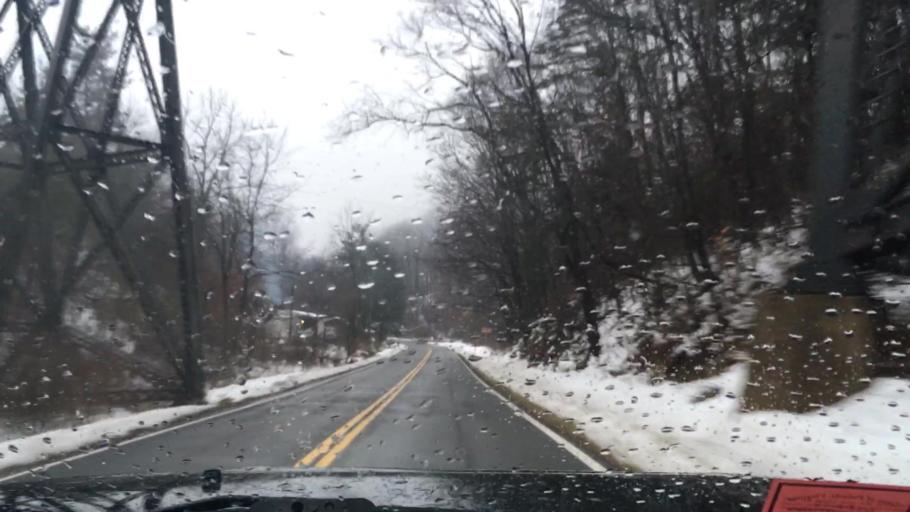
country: US
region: Virginia
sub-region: Pulaski County
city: Pulaski
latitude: 37.0283
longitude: -80.7253
